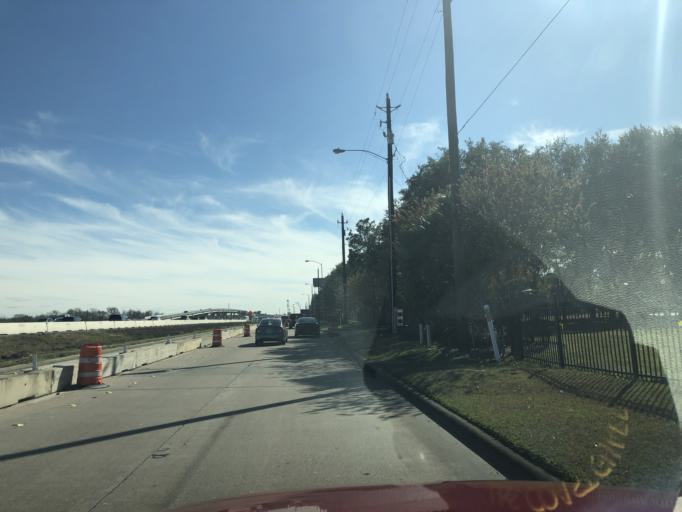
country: US
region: Texas
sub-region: Harris County
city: Webster
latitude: 29.5154
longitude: -95.1220
